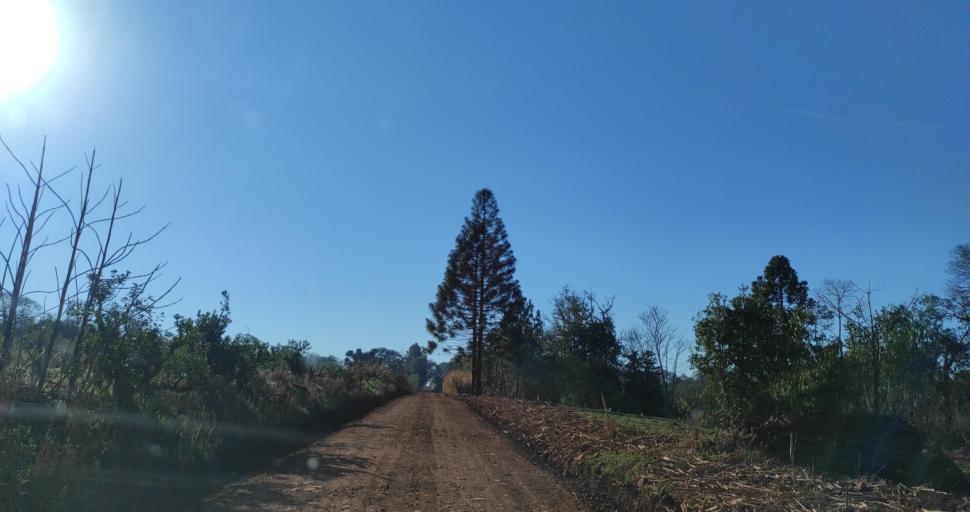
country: AR
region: Misiones
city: Capiovi
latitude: -26.8801
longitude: -55.0214
